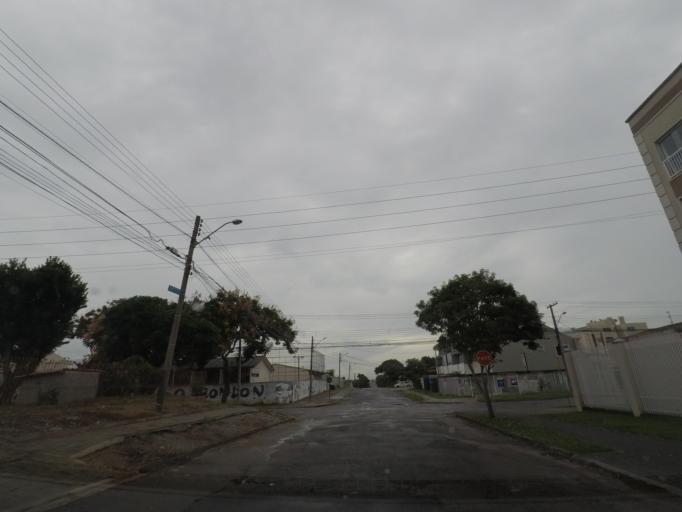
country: BR
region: Parana
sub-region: Curitiba
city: Curitiba
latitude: -25.4746
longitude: -49.3104
